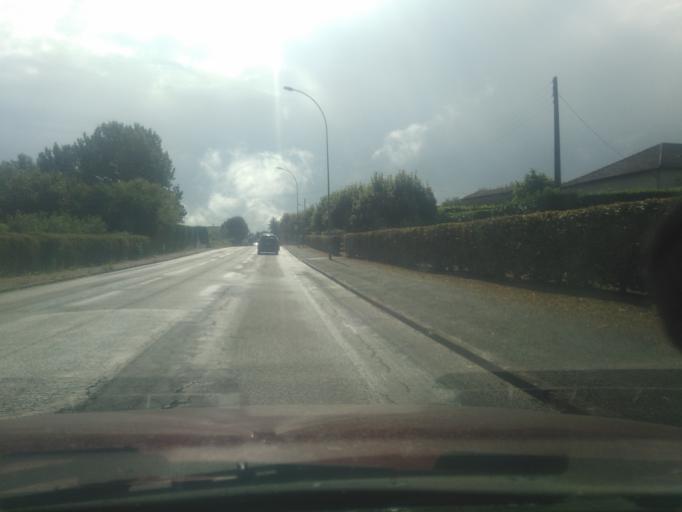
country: FR
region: Poitou-Charentes
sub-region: Departement des Deux-Sevres
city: Parthenay
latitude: 46.6345
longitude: -0.2546
